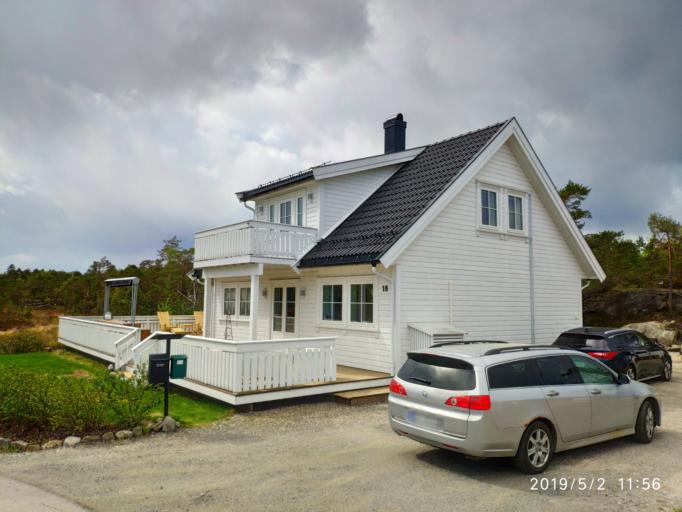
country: NO
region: Telemark
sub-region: Kragero
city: Kragero
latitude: 58.8464
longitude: 9.3886
